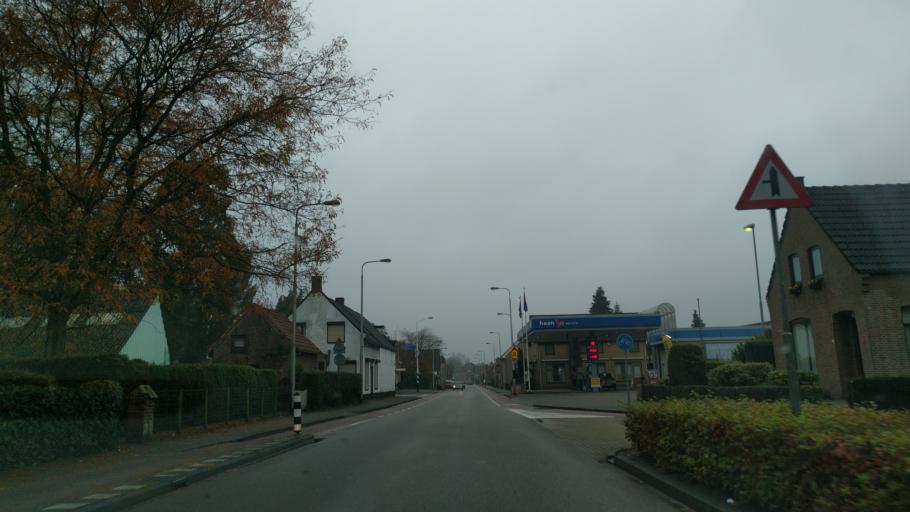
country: NL
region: North Brabant
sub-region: Gemeente Rucphen
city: Rucphen
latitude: 51.5322
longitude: 4.5654
